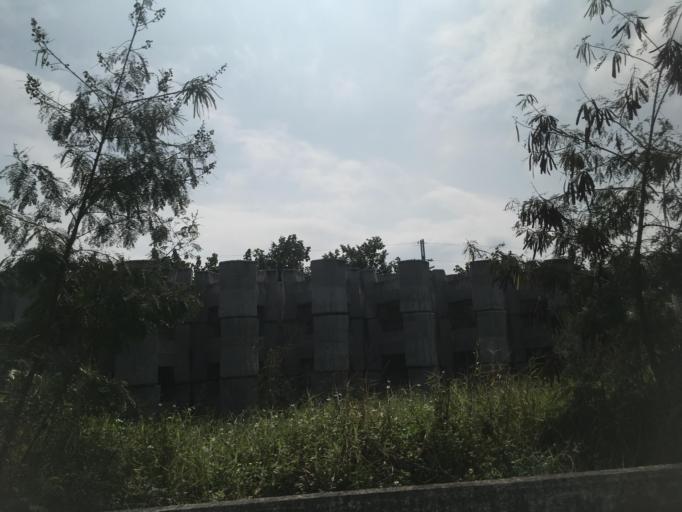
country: TW
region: Taiwan
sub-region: Yunlin
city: Douliu
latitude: 23.6947
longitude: 120.4479
